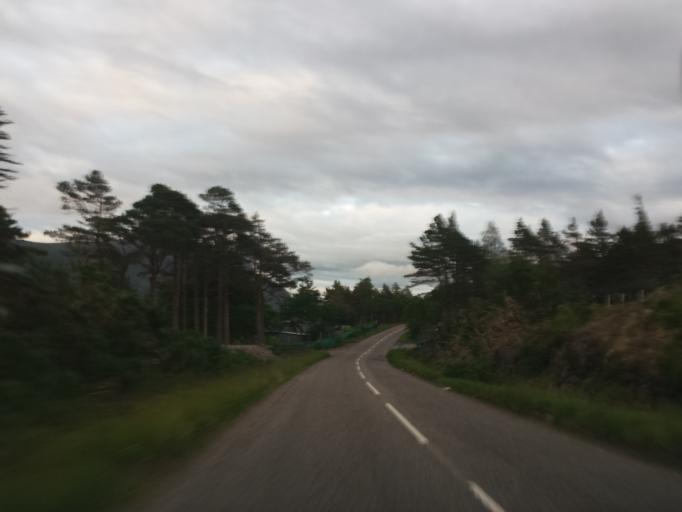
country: GB
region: Scotland
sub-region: Highland
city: Ullapool
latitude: 57.5266
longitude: -5.5819
